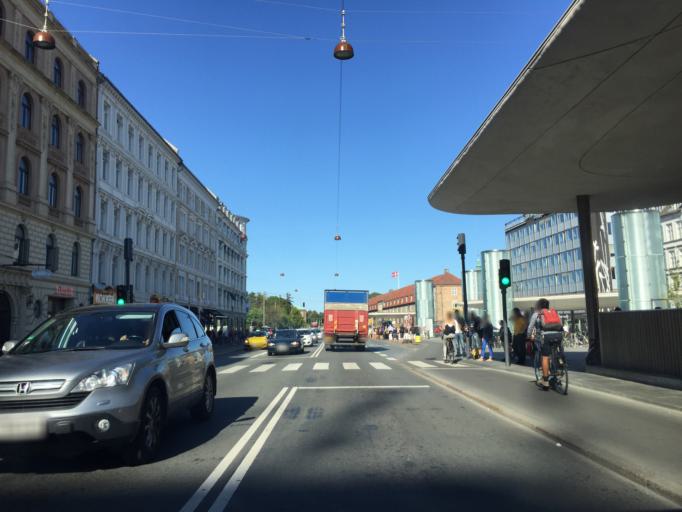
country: DK
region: Capital Region
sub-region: Kobenhavn
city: Copenhagen
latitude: 55.6838
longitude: 12.5722
